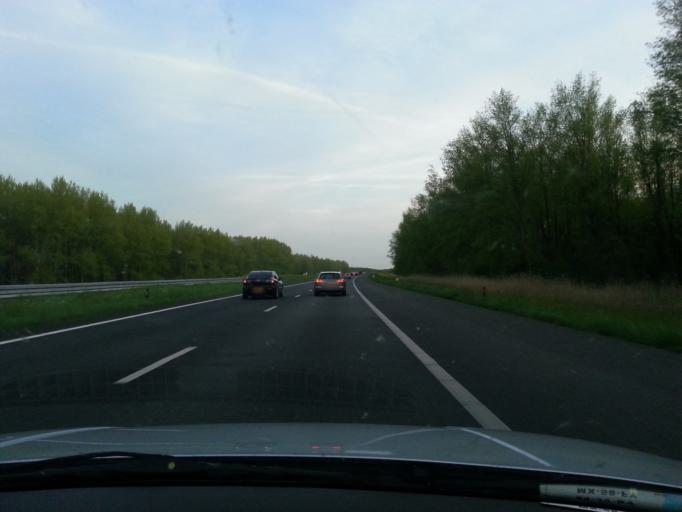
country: NL
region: Flevoland
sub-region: Gemeente Lelystad
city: Lelystad
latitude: 52.5101
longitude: 5.5332
